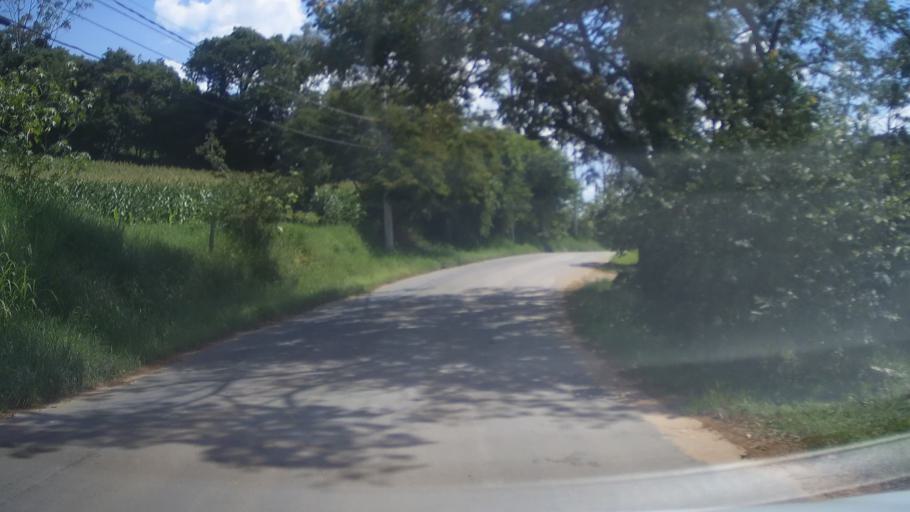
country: BR
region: Sao Paulo
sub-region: Jarinu
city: Jarinu
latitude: -23.1247
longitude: -46.8061
